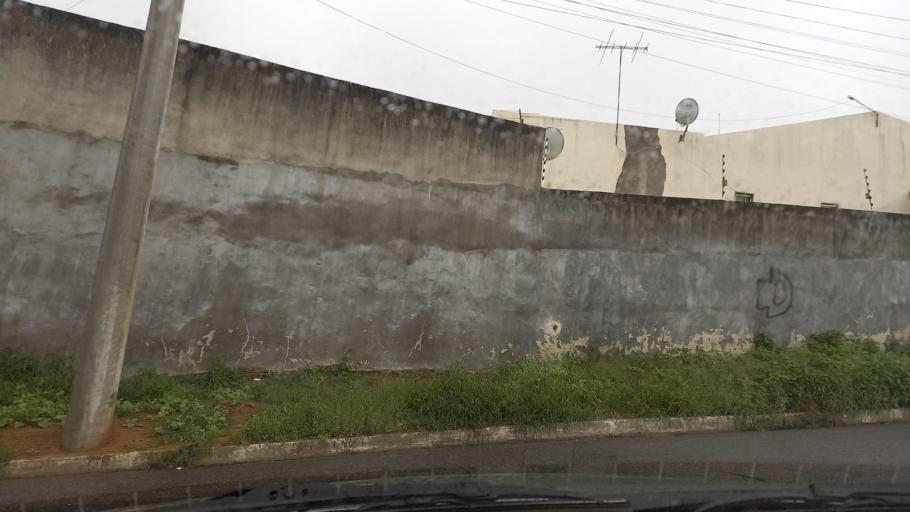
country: BR
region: Pernambuco
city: Garanhuns
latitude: -8.8863
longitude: -36.4973
